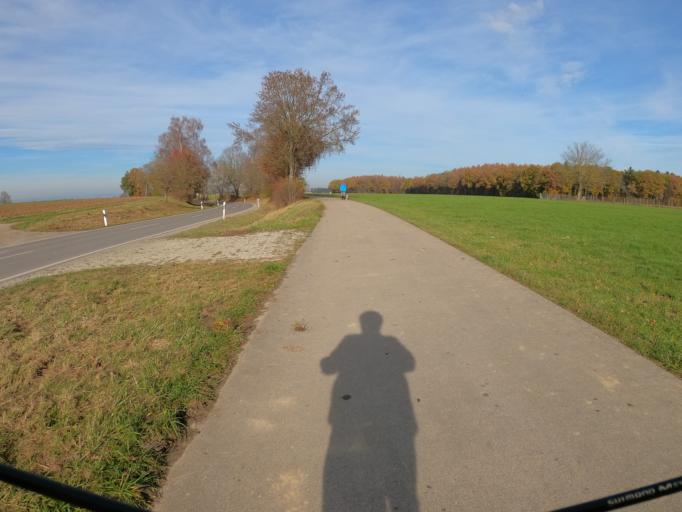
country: DE
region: Bavaria
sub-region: Swabia
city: Leipheim
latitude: 48.4022
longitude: 10.2012
